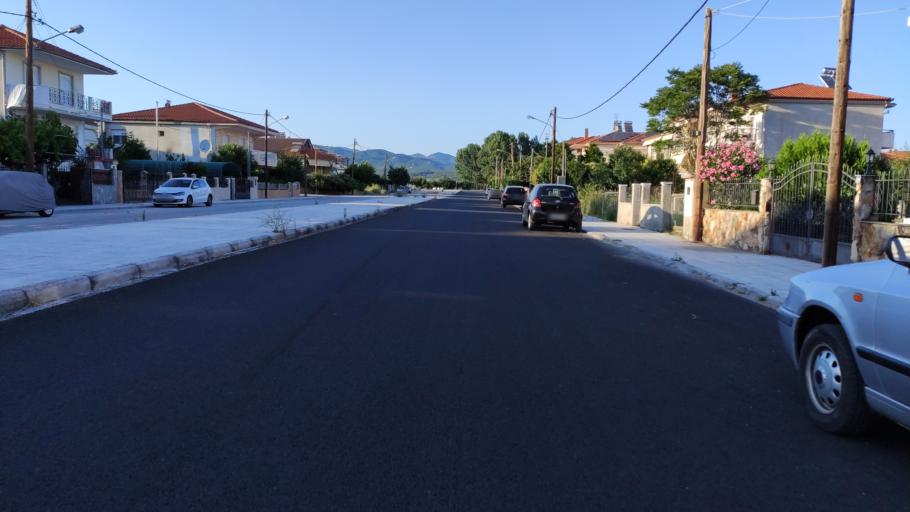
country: GR
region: East Macedonia and Thrace
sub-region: Nomos Rodopis
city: Komotini
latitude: 41.1308
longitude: 25.3970
